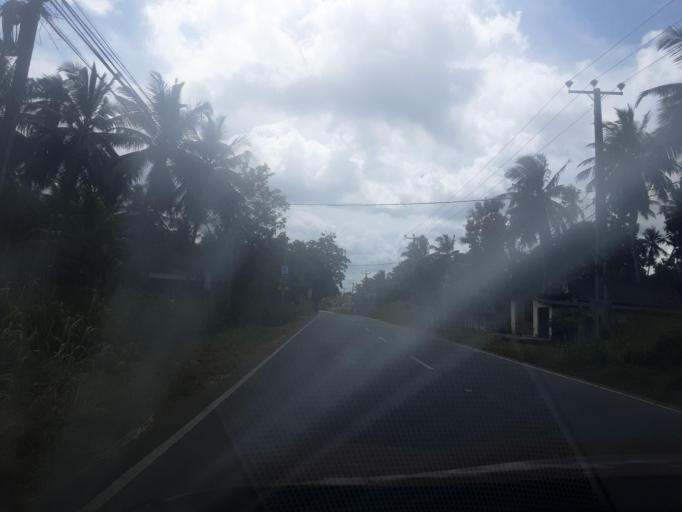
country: LK
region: North Western
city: Kuliyapitiya
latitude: 7.4781
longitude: 80.0023
